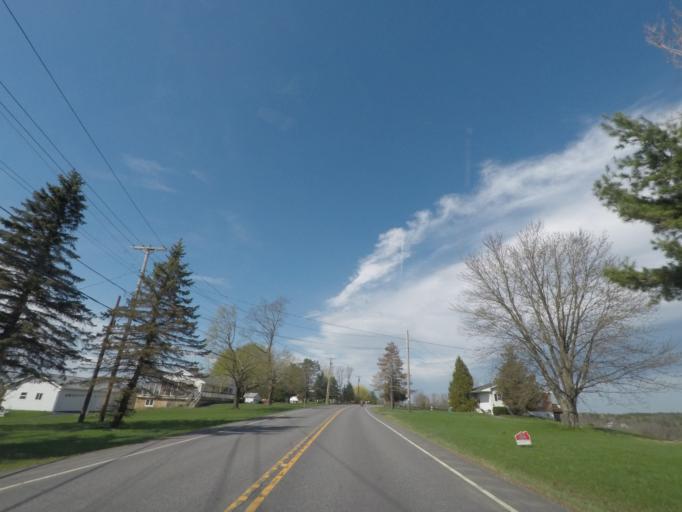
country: US
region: New York
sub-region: Greene County
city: Cairo
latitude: 42.4033
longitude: -74.0272
